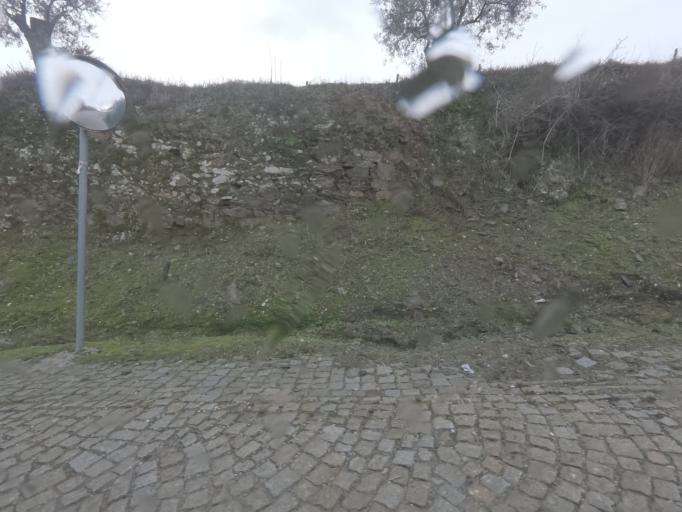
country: PT
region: Vila Real
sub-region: Peso da Regua
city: Peso da Regua
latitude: 41.1660
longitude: -7.7236
